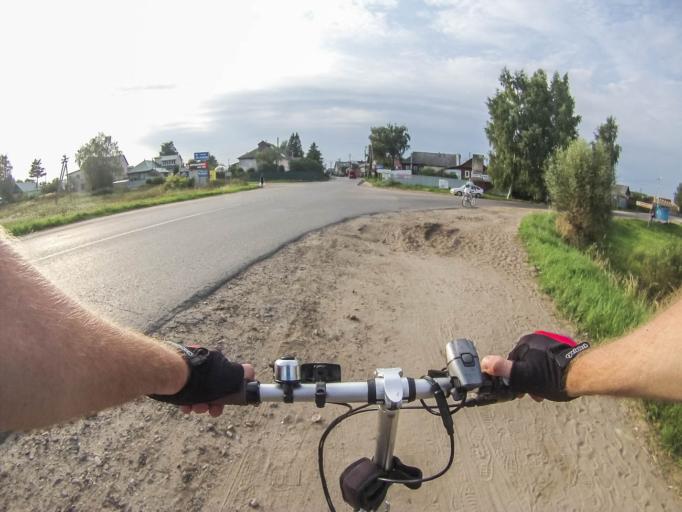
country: RU
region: Kostroma
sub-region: Kostromskoy Rayon
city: Kostroma
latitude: 57.7895
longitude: 40.8619
